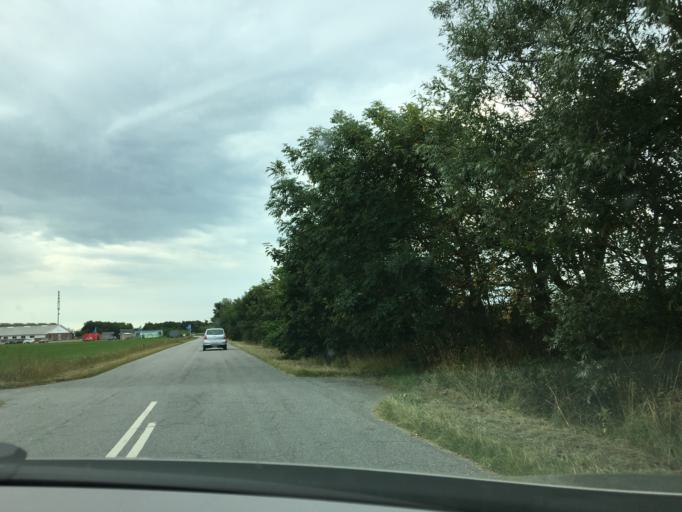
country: DK
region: South Denmark
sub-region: Varde Kommune
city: Oksbol
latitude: 55.8459
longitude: 8.2910
